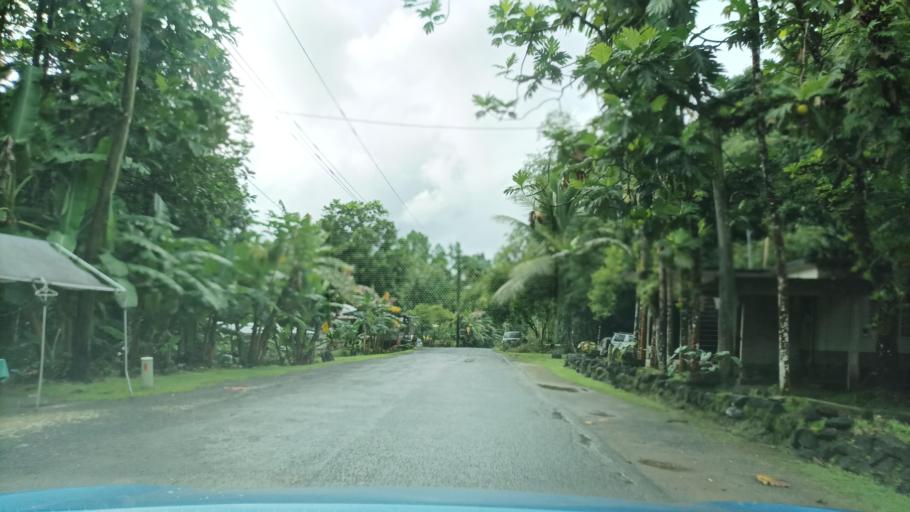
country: FM
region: Pohnpei
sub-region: Kolonia Municipality
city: Kolonia
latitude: 6.9425
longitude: 158.2755
